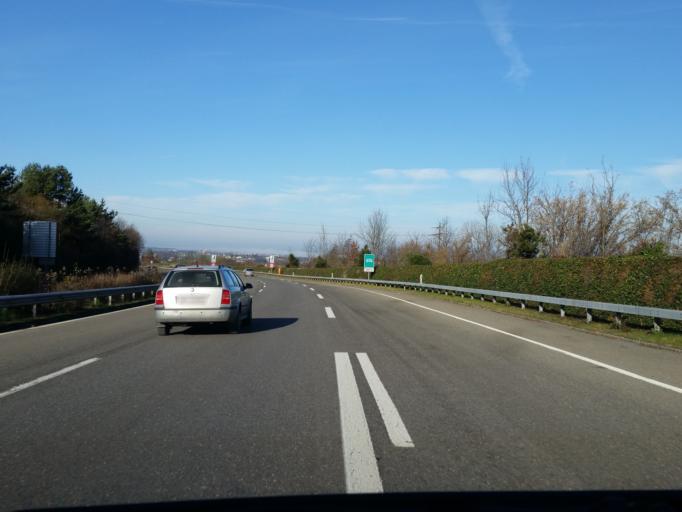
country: CH
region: Saint Gallen
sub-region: Wahlkreis Rorschach
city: Horn
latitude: 47.4831
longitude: 9.4430
